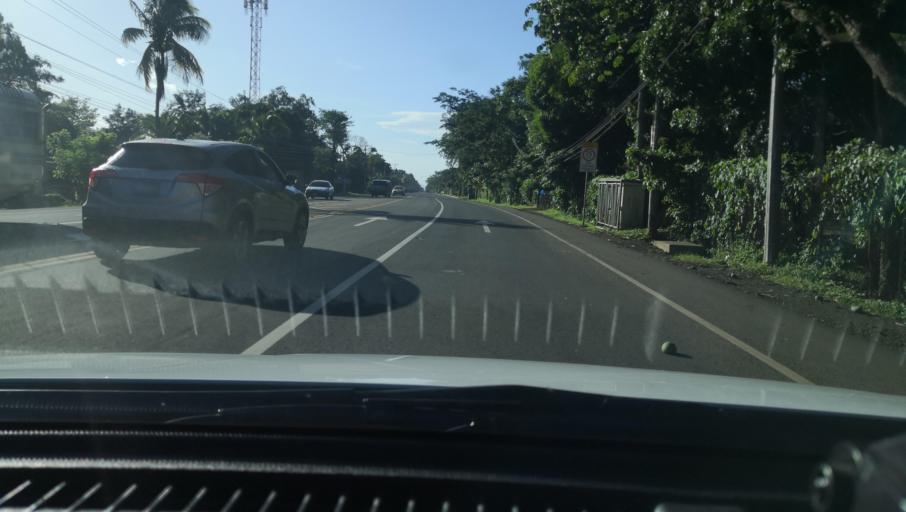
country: NI
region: Carazo
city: Jinotepe
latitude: 11.8281
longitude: -86.1738
